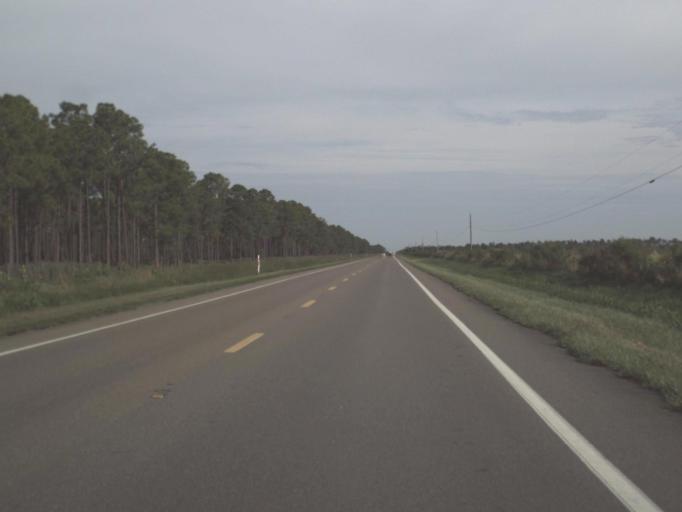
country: US
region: Florida
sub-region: Lee County
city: Olga
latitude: 26.8751
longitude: -81.7599
